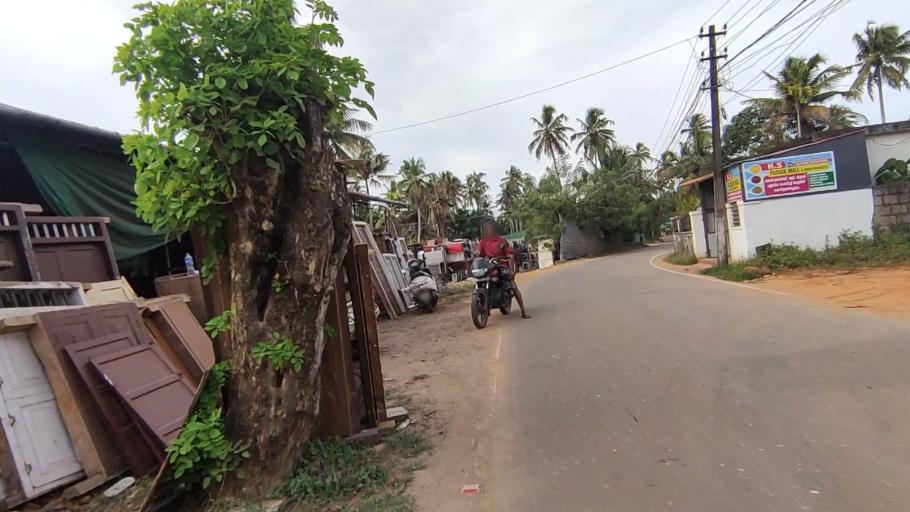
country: IN
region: Kerala
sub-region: Kottayam
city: Kottayam
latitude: 9.5908
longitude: 76.4909
